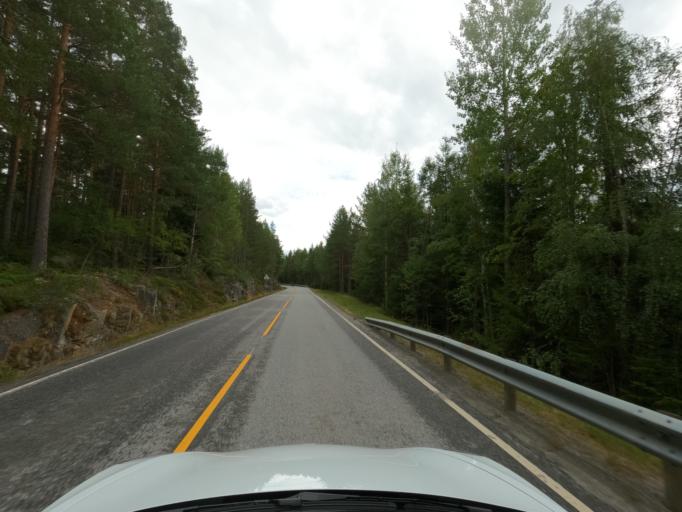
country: NO
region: Telemark
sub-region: Notodden
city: Notodden
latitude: 59.7313
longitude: 9.2402
